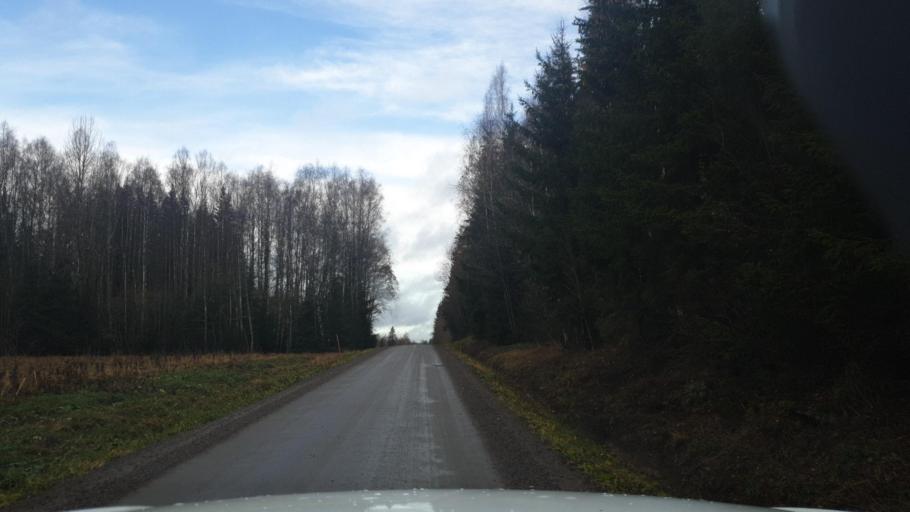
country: NO
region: Hedmark
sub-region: Eidskog
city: Skotterud
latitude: 59.8596
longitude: 11.9845
